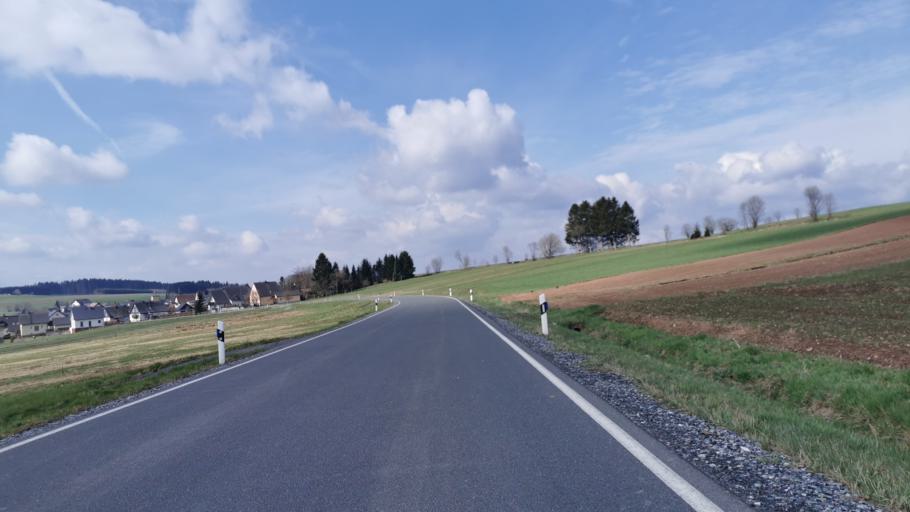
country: DE
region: Bavaria
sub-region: Upper Franconia
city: Tettau
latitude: 50.4282
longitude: 11.2942
